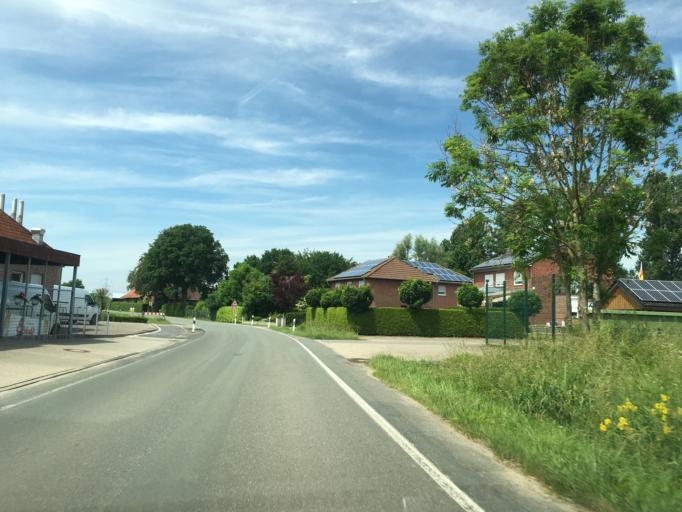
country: DE
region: North Rhine-Westphalia
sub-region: Regierungsbezirk Munster
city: Nordwalde
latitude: 52.1160
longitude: 7.4547
